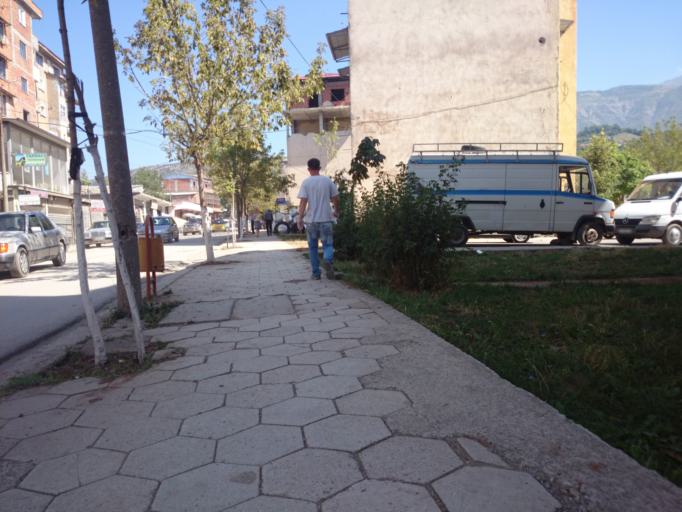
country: AL
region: Diber
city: Peshkopi
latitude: 41.6825
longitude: 20.4260
